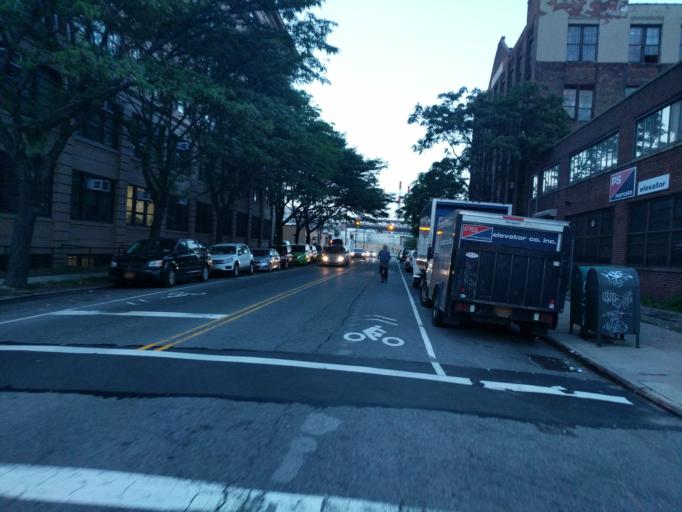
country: US
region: New York
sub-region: Queens County
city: Long Island City
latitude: 40.7493
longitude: -73.9494
